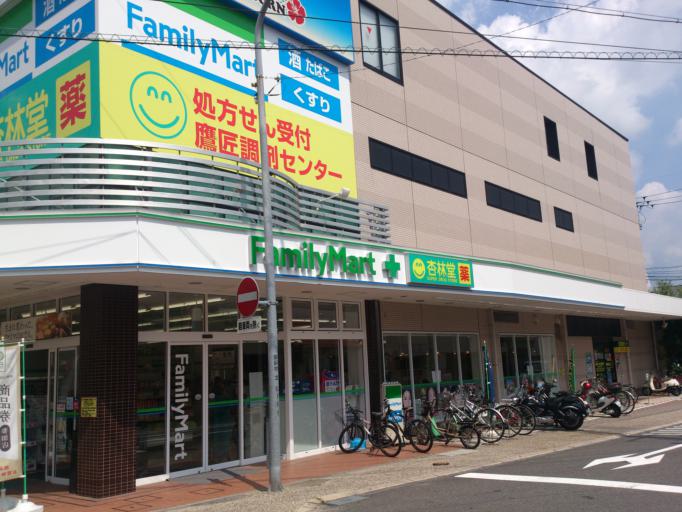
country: JP
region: Shizuoka
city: Shizuoka-shi
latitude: 34.9762
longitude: 138.3894
